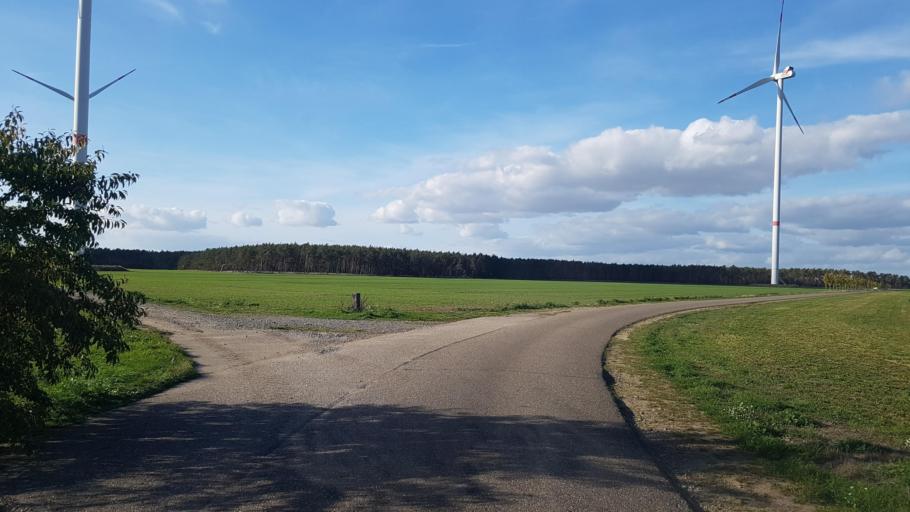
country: DE
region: Brandenburg
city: Bad Liebenwerda
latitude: 51.4659
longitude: 13.3308
